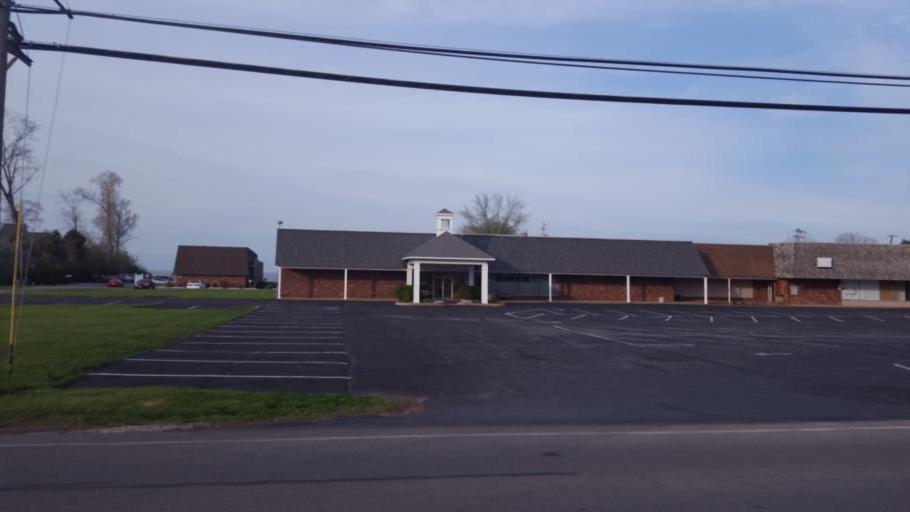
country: US
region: Ohio
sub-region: Erie County
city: Huron
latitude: 41.3991
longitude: -82.5621
